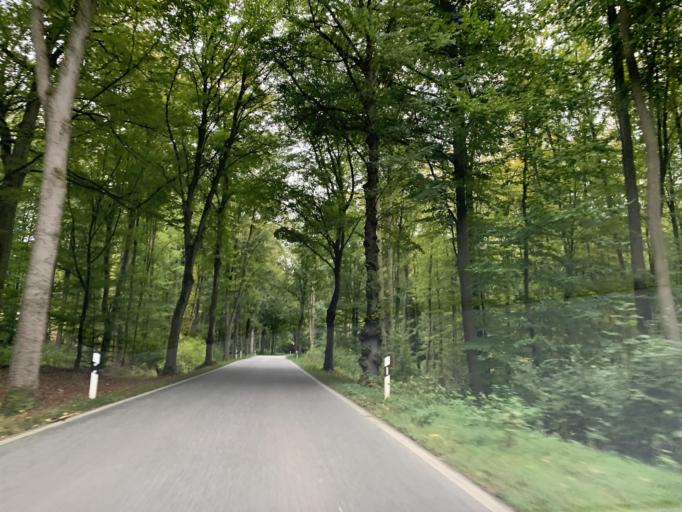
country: DE
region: Mecklenburg-Vorpommern
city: Burg Stargard
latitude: 53.4852
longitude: 13.3005
